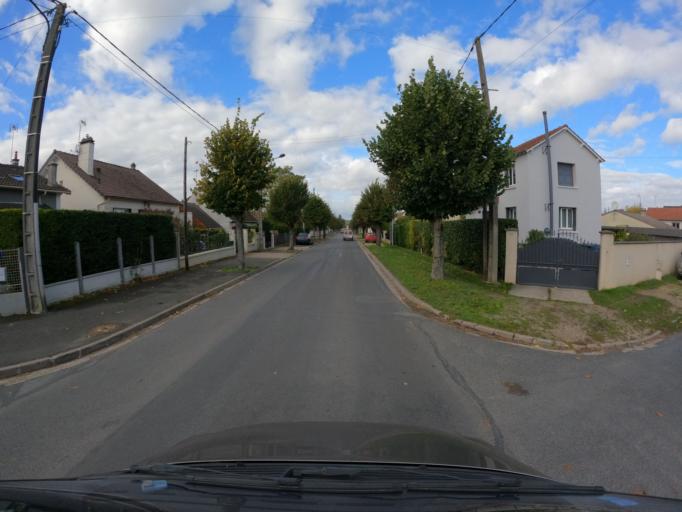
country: FR
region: Ile-de-France
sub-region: Departement de Seine-et-Marne
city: Montry
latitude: 48.8865
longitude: 2.8330
